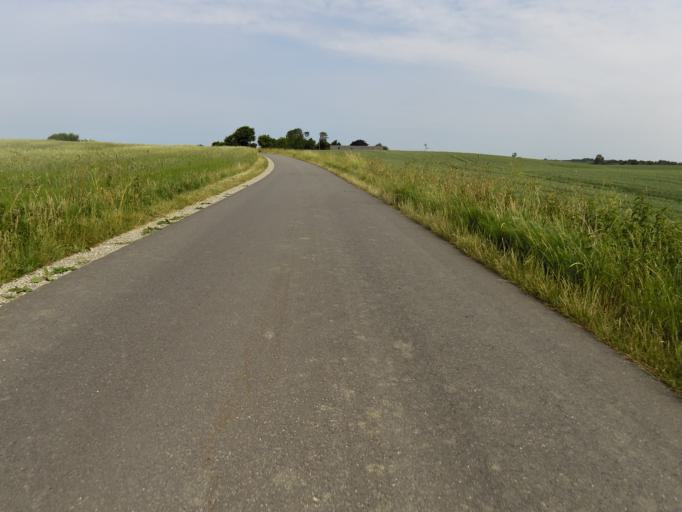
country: DK
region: Central Jutland
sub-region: Holstebro Kommune
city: Holstebro
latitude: 56.4305
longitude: 8.6687
